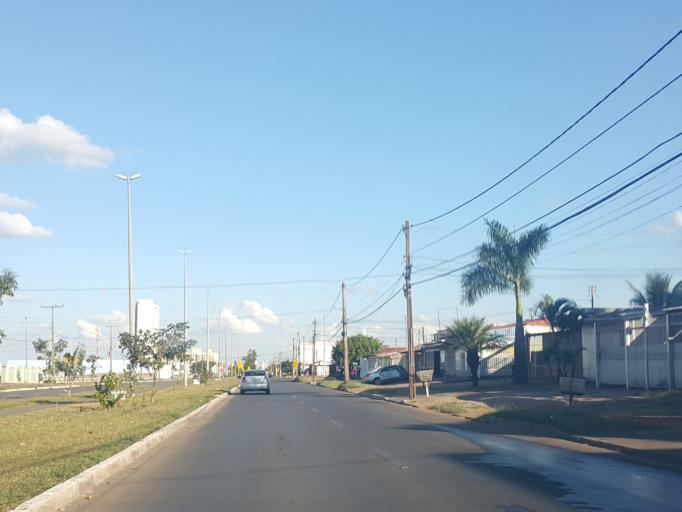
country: BR
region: Federal District
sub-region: Brasilia
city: Brasilia
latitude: -15.8259
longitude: -48.0932
